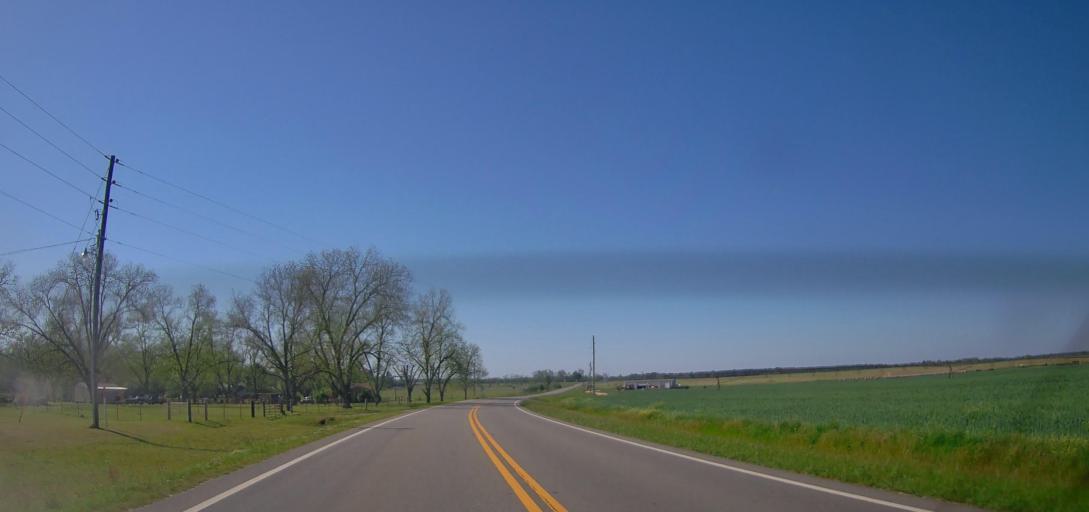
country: US
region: Georgia
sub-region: Pulaski County
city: Hawkinsville
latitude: 32.1353
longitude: -83.5069
